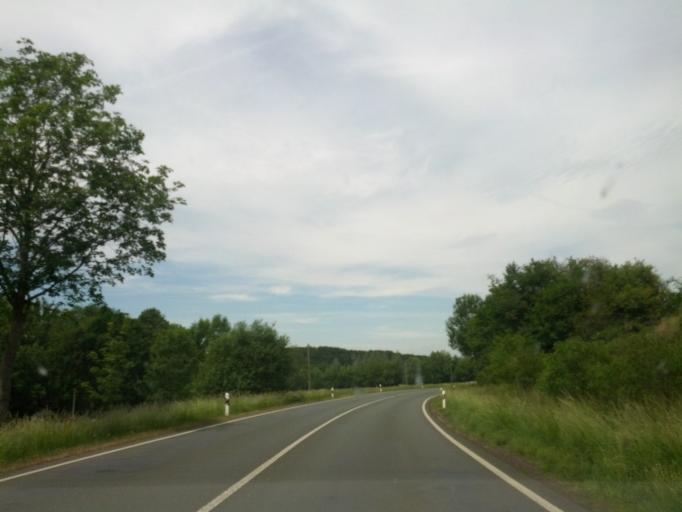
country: DE
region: Thuringia
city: Tabarz
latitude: 50.8925
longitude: 10.5179
